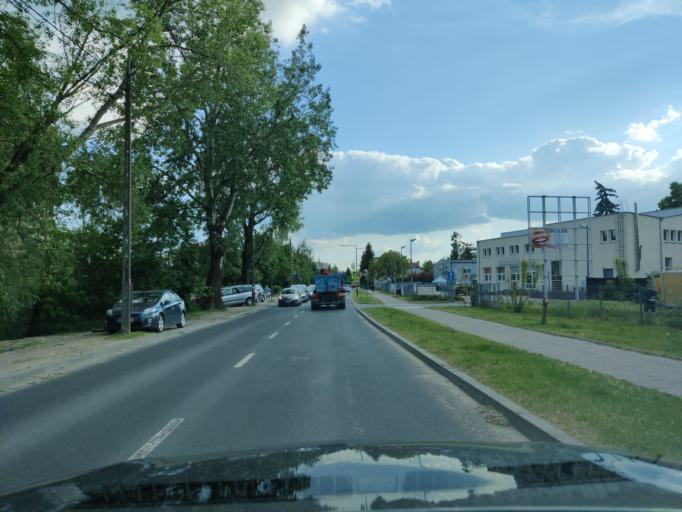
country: PL
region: Masovian Voivodeship
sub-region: Powiat piaseczynski
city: Konstancin-Jeziorna
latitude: 52.0976
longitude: 21.1243
